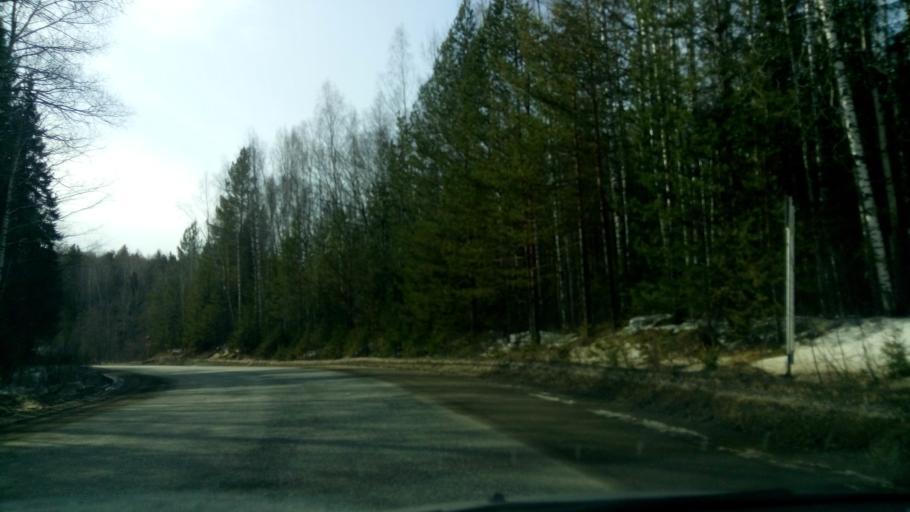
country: RU
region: Sverdlovsk
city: Chernoistochinsk
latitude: 57.6998
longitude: 59.7626
